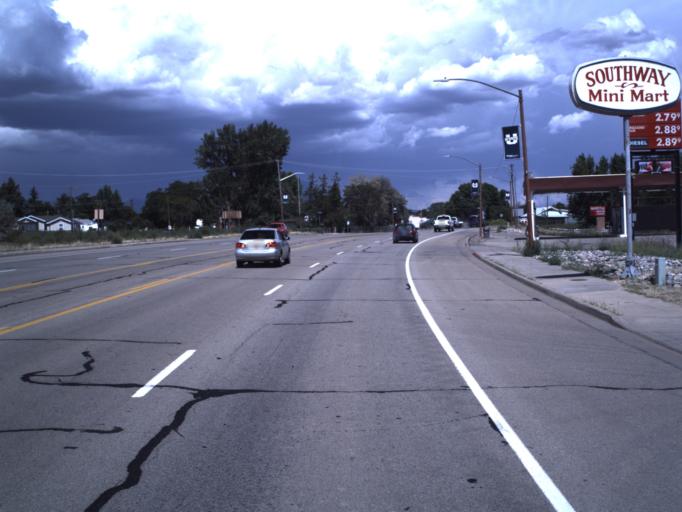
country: US
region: Utah
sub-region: San Juan County
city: Blanding
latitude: 37.6157
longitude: -109.4788
